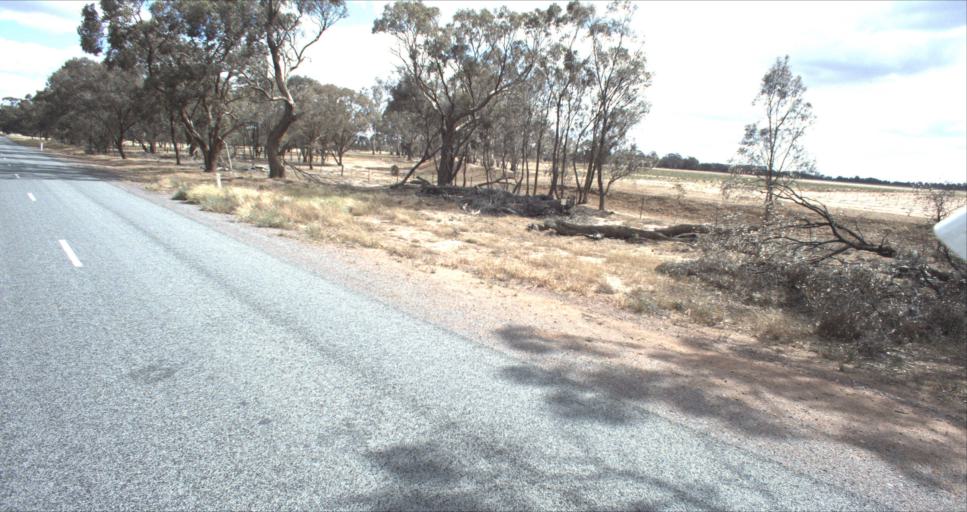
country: AU
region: New South Wales
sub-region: Leeton
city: Leeton
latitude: -34.6638
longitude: 146.3488
